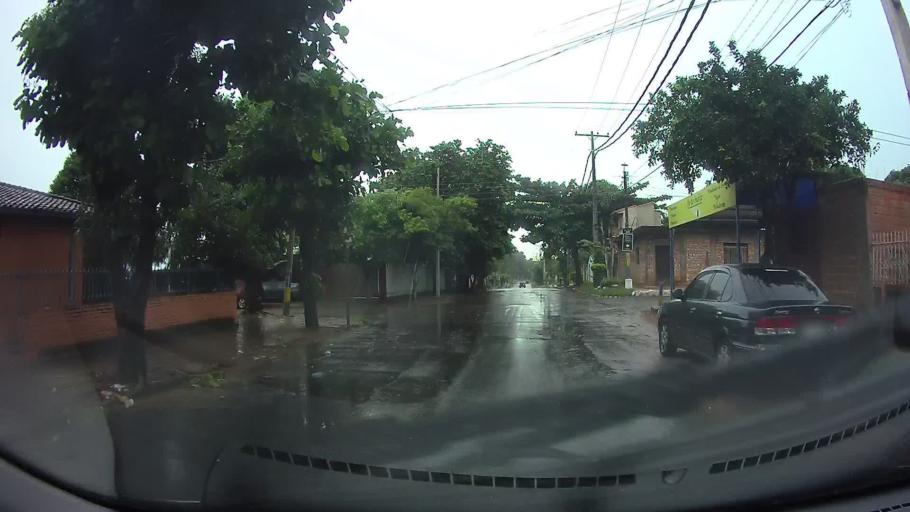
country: PY
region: Central
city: San Lorenzo
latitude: -25.2679
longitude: -57.4803
